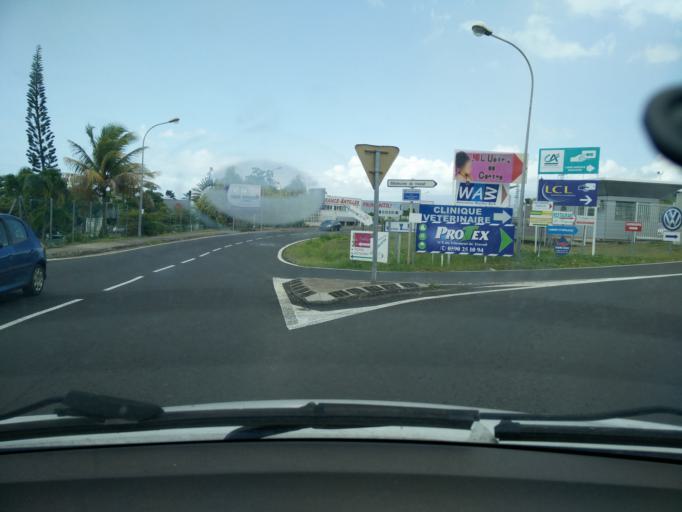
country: GP
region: Guadeloupe
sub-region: Guadeloupe
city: Baie-Mahault
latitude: 16.2401
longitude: -61.5829
